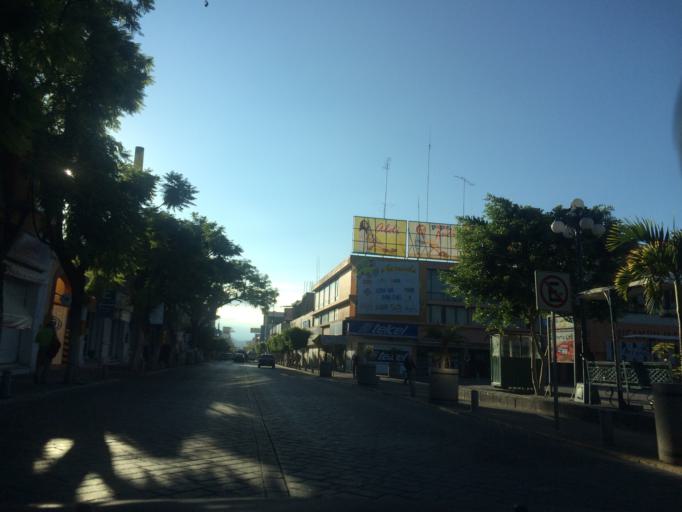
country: MX
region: Puebla
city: Tehuacan
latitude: 18.4630
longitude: -97.3925
